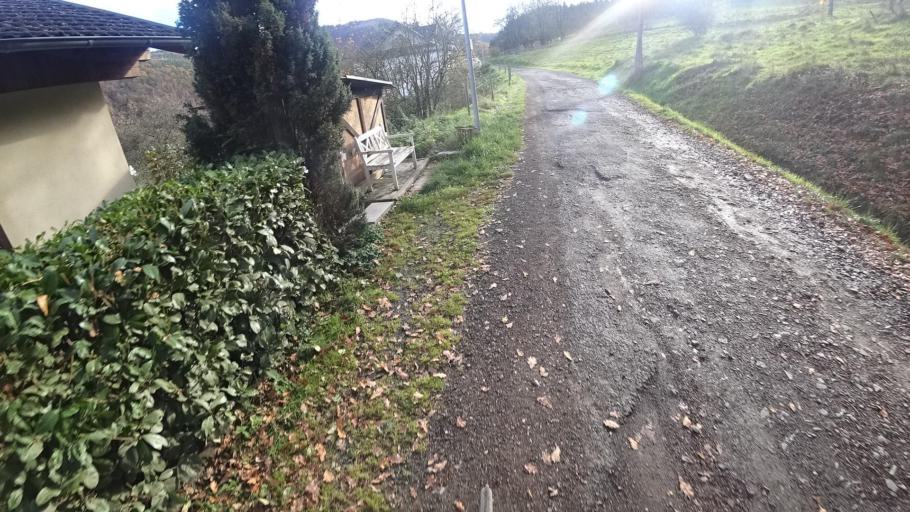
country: DE
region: Rheinland-Pfalz
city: Honningen
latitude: 50.4668
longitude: 6.9455
